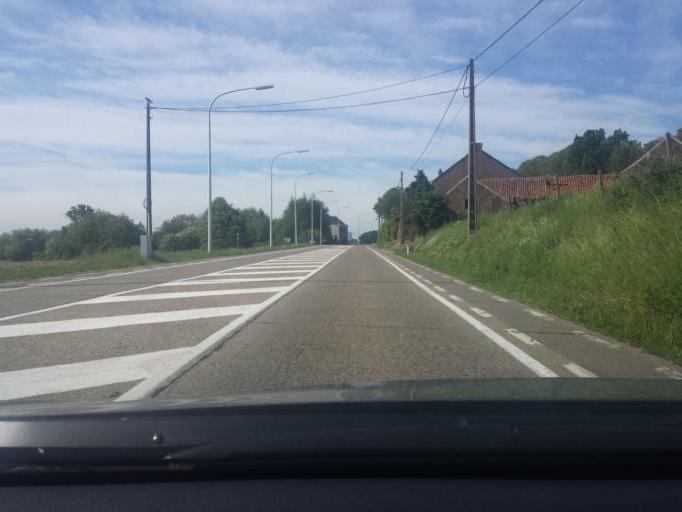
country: BE
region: Flanders
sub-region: Provincie Vlaams-Brabant
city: Diest
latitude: 50.9627
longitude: 5.0257
